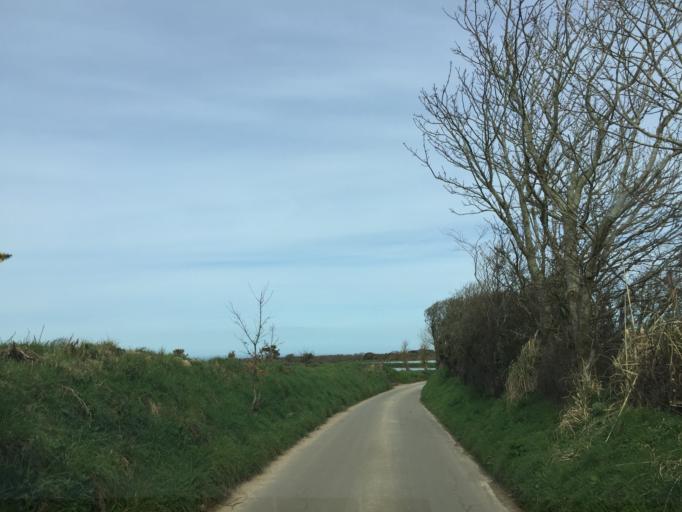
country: JE
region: St Helier
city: Saint Helier
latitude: 49.2448
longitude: -2.1738
